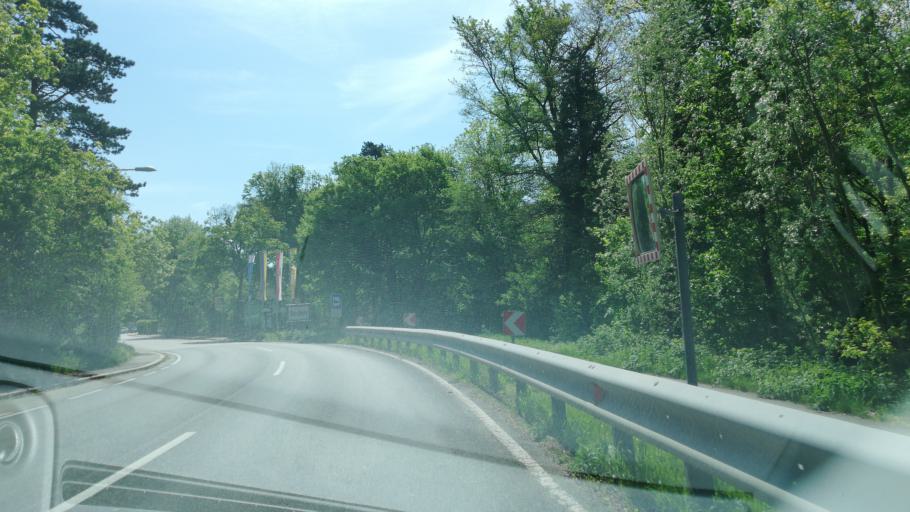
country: AT
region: Lower Austria
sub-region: Politischer Bezirk Baden
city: Baden
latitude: 48.0151
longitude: 16.1981
